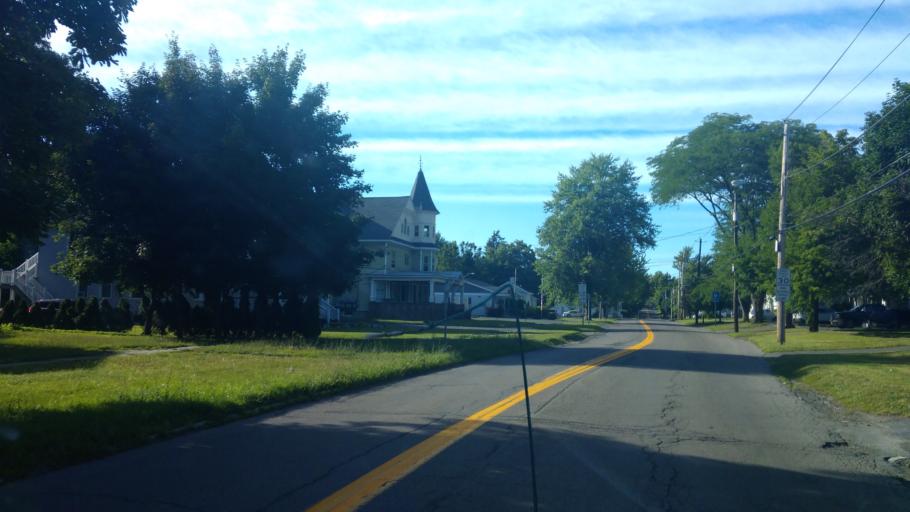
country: US
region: New York
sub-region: Wayne County
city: Lyons
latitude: 43.0680
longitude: -76.9893
